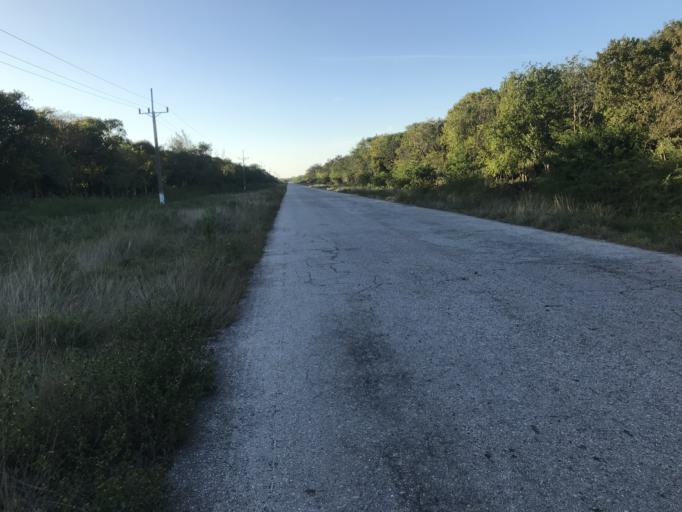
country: CU
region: Cienfuegos
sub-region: Municipio de Aguada de Pasajeros
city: Aguada de Pasajeros
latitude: 22.0766
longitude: -81.0634
